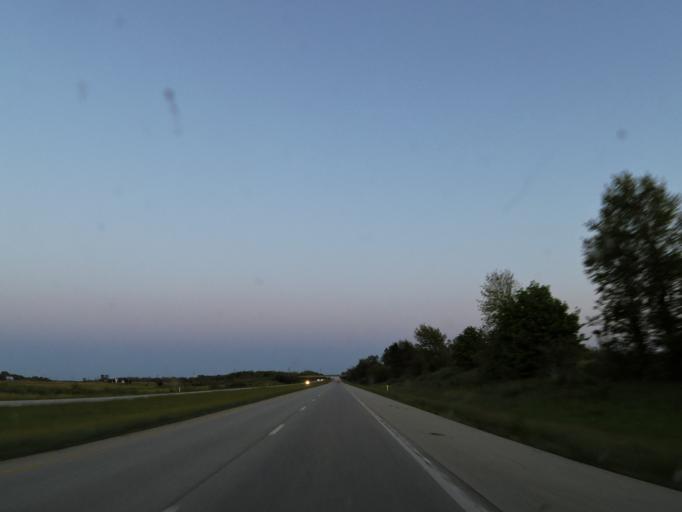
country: US
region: Indiana
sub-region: Boone County
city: Thorntown
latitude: 39.9697
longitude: -86.6573
